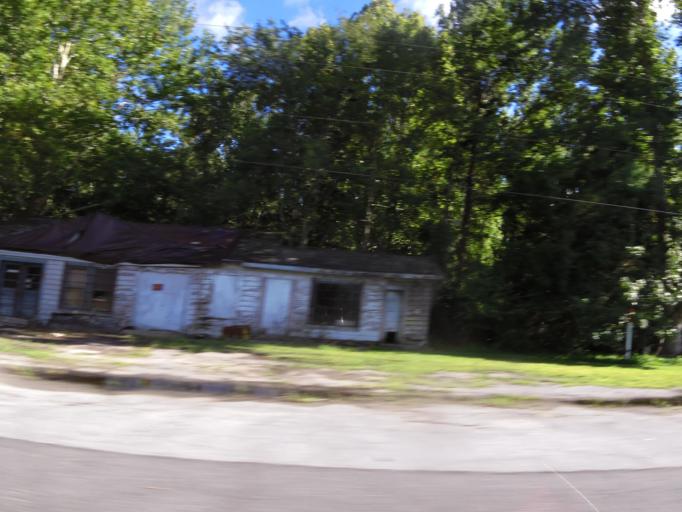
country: US
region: Georgia
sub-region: Camden County
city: Woodbine
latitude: 31.1069
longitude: -81.6734
